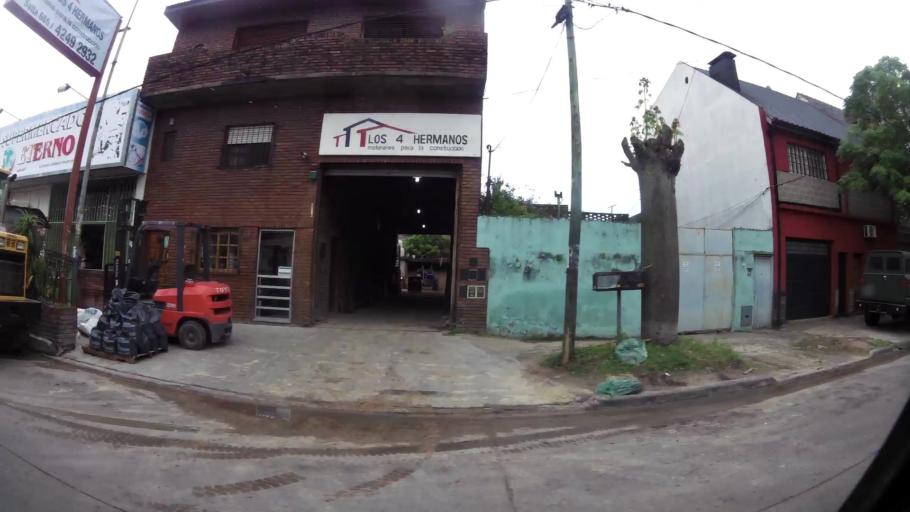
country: AR
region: Buenos Aires
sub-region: Partido de Lanus
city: Lanus
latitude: -34.7007
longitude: -58.3740
